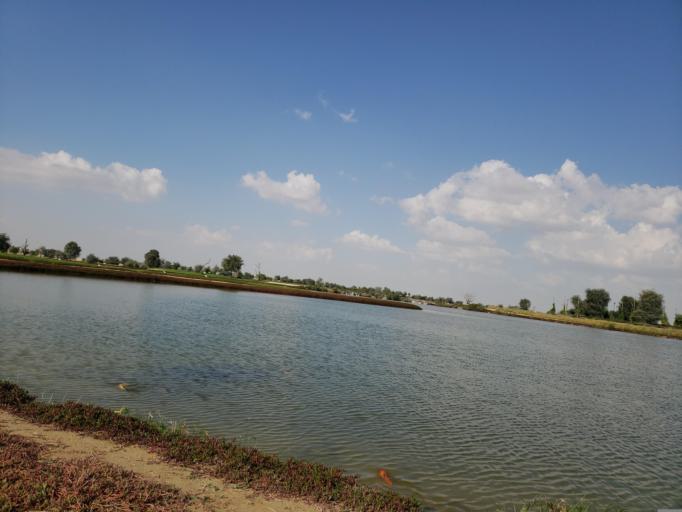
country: AE
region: Dubai
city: Dubai
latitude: 24.8524
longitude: 55.2485
